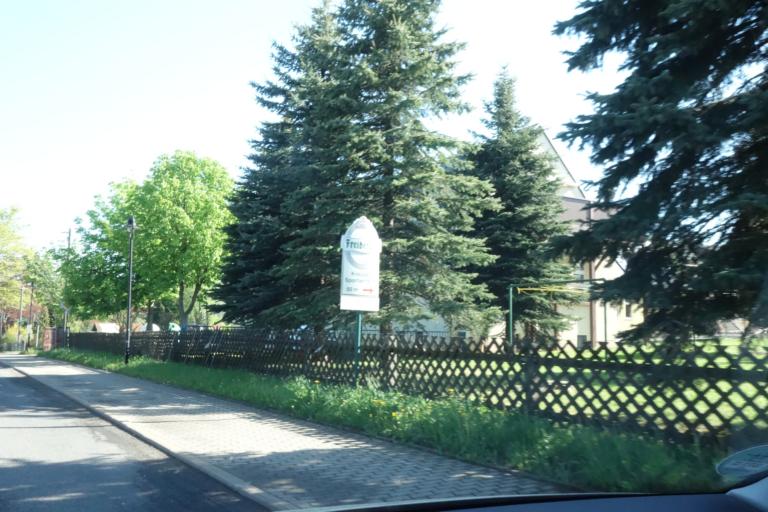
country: DE
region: Saxony
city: Pfaffroda
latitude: 50.7327
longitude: 13.3353
